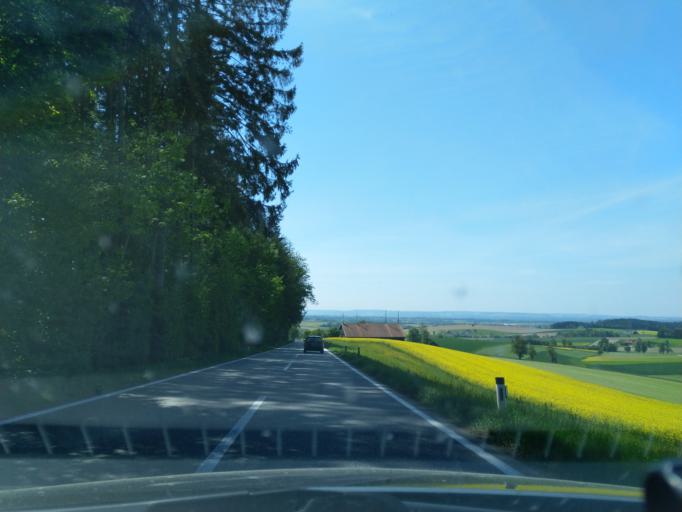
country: DE
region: Bavaria
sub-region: Lower Bavaria
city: Bad Fussing
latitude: 48.2774
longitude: 13.3943
